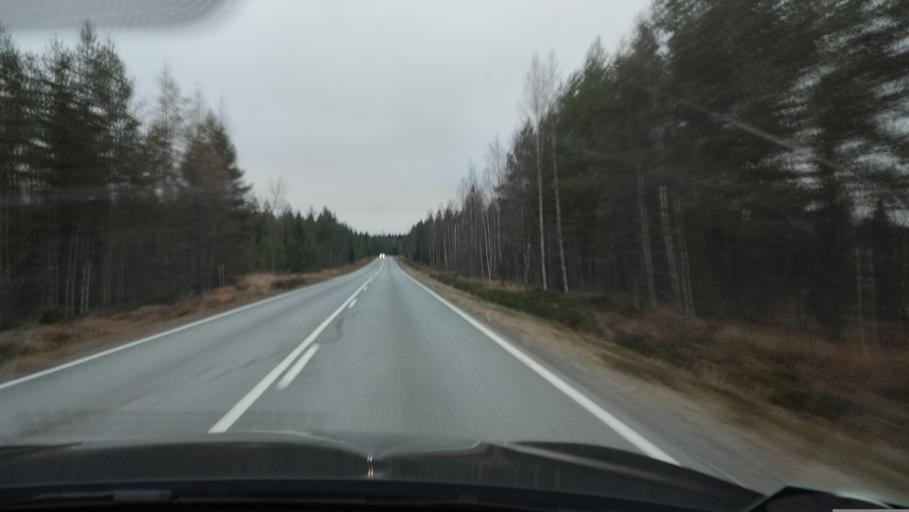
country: FI
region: Southern Ostrobothnia
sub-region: Suupohja
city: Karijoki
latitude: 62.3266
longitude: 21.8949
